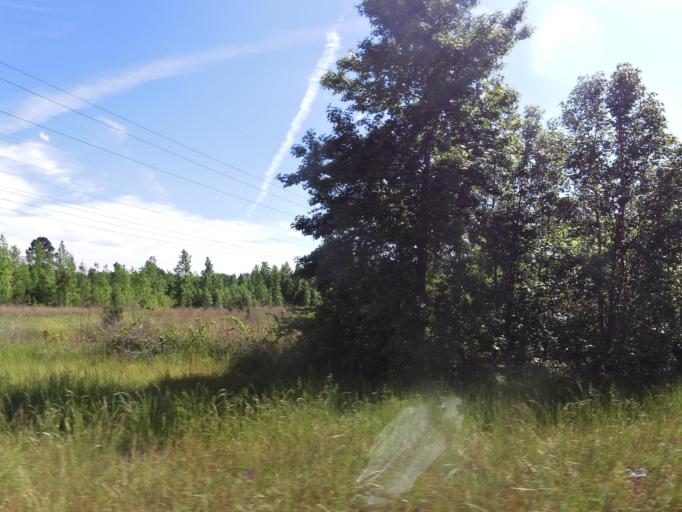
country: US
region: South Carolina
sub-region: Bamberg County
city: Denmark
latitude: 33.3327
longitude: -81.1577
